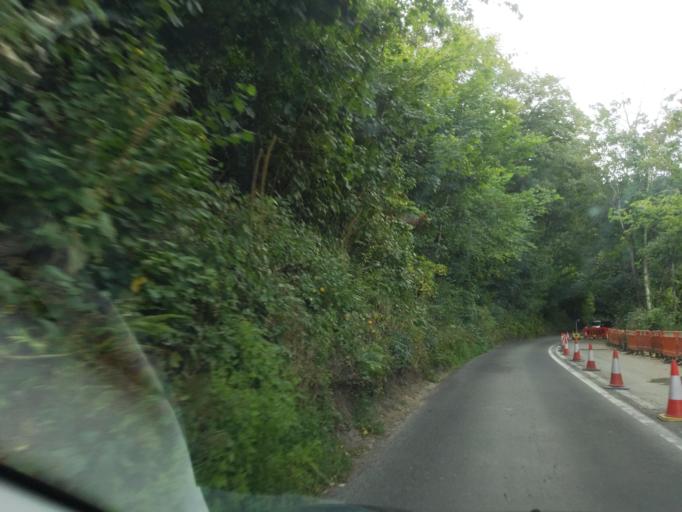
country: GB
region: England
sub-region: Devon
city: Winkleigh
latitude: 50.9575
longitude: -3.9651
